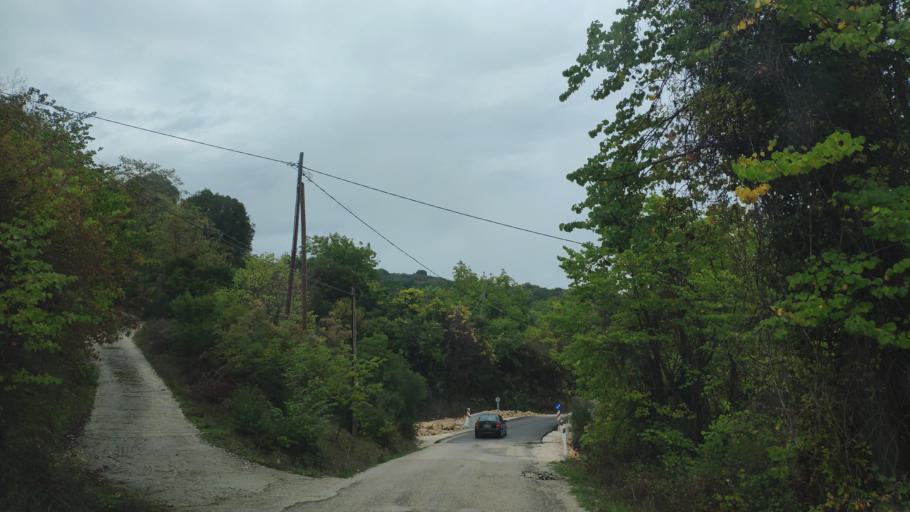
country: GR
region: Epirus
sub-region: Nomos Thesprotias
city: Paramythia
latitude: 39.4657
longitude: 20.6719
